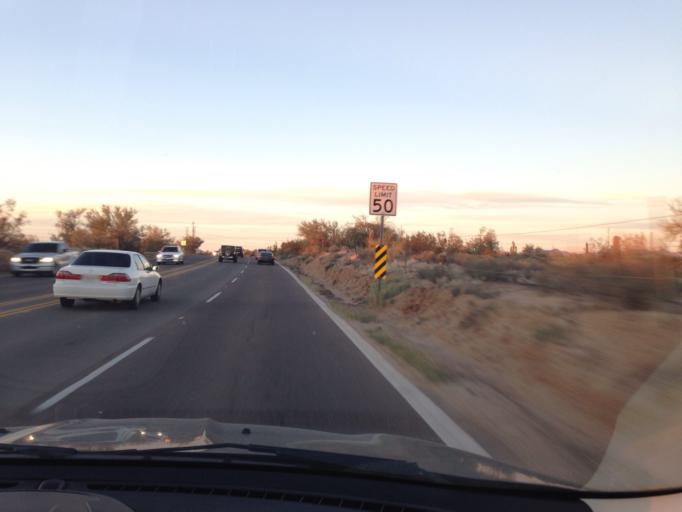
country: US
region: Arizona
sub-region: Maricopa County
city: Carefree
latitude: 33.7025
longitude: -111.9690
